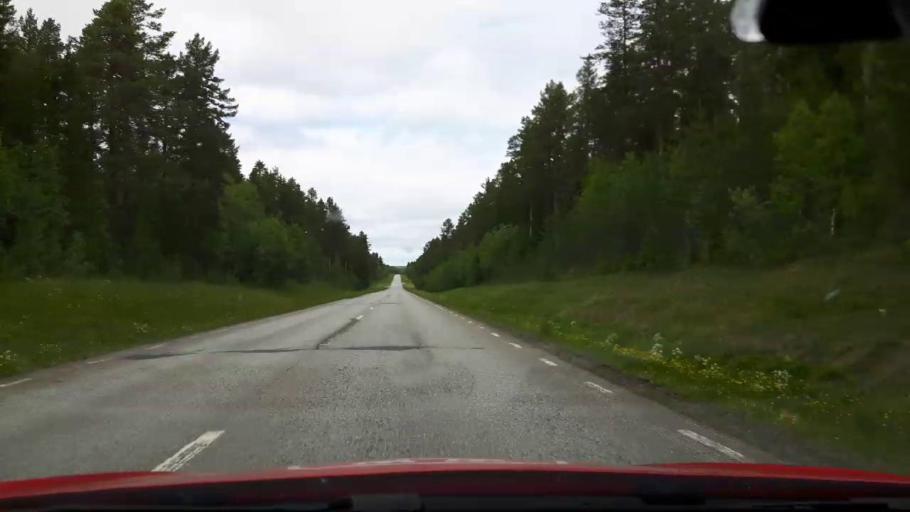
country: SE
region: Jaemtland
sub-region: Krokoms Kommun
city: Krokom
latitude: 63.4382
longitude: 14.4971
